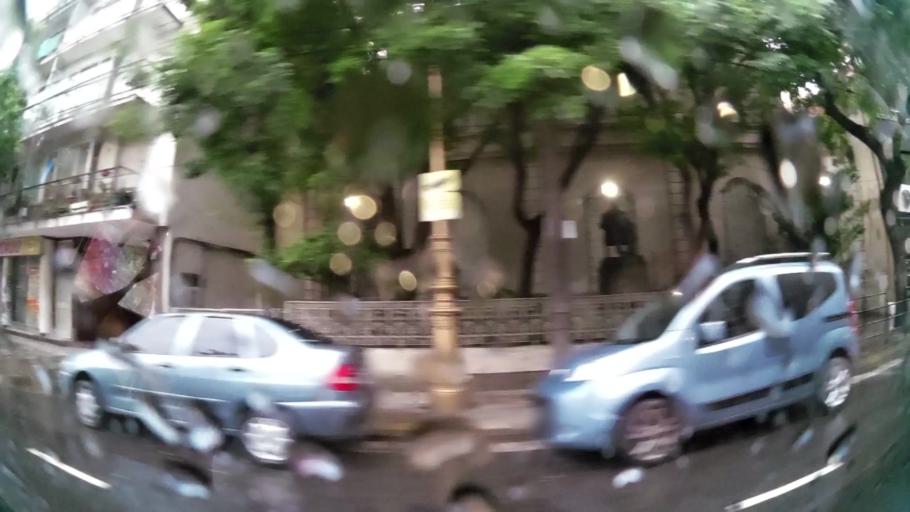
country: AR
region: Buenos Aires F.D.
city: Buenos Aires
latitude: -34.6338
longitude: -58.3756
